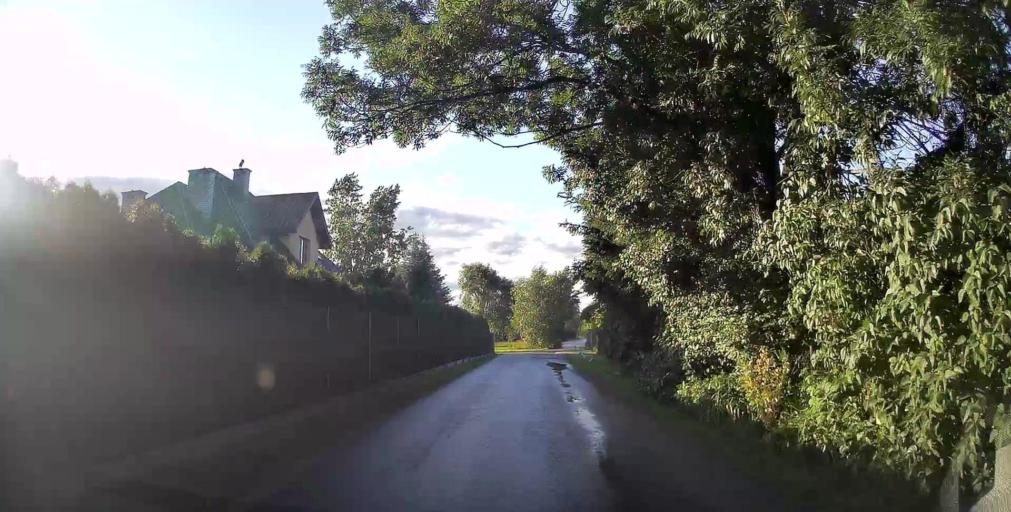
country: PL
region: Masovian Voivodeship
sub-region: Powiat grojecki
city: Goszczyn
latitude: 51.7589
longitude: 20.8807
